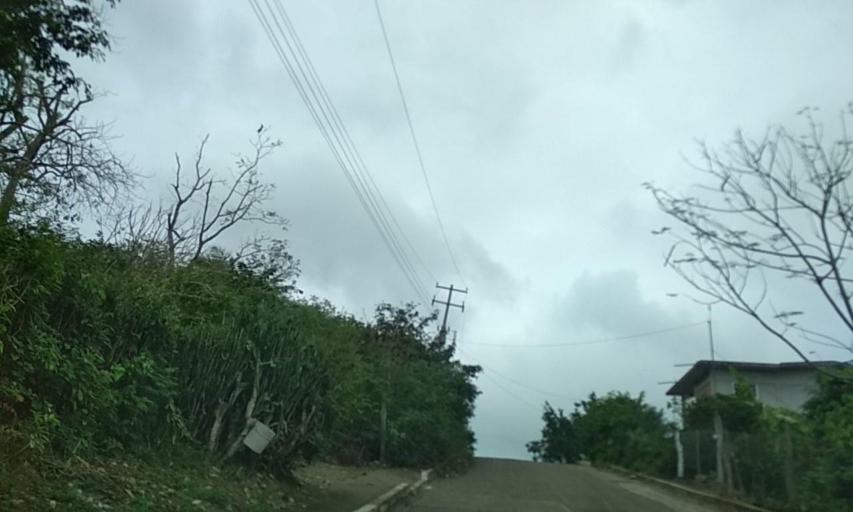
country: MX
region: Veracruz
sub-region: Papantla
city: El Chote
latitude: 20.3797
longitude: -97.3510
